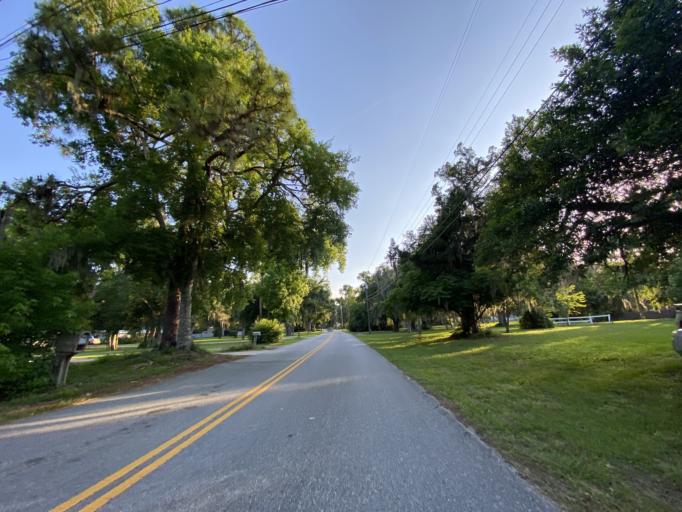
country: US
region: Florida
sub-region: Volusia County
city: Port Orange
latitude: 29.1448
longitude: -81.0022
